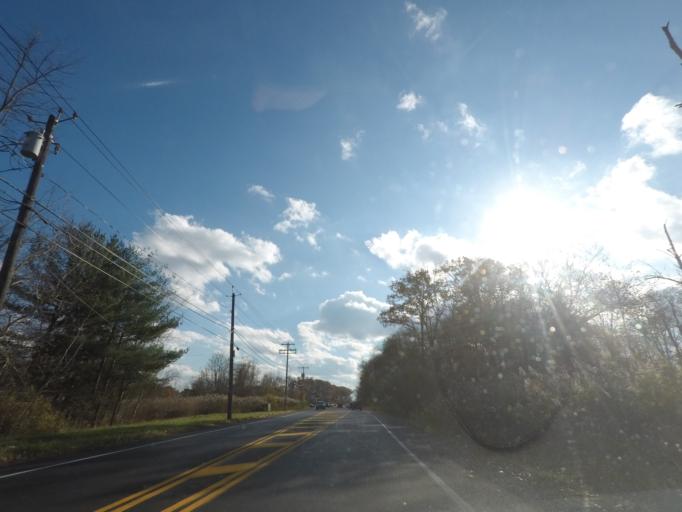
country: US
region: New York
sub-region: Schenectady County
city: Niskayuna
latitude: 42.7852
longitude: -73.8931
